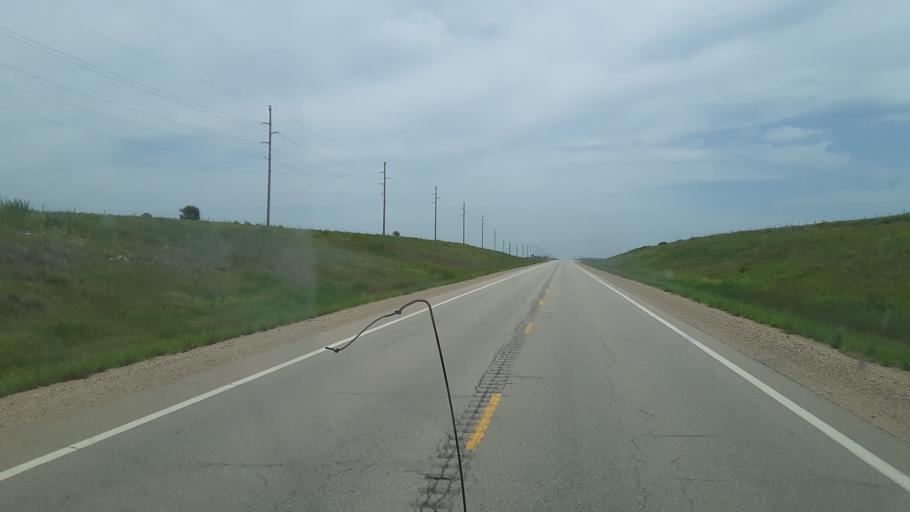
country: US
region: Kansas
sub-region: Greenwood County
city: Eureka
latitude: 37.8371
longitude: -96.0374
